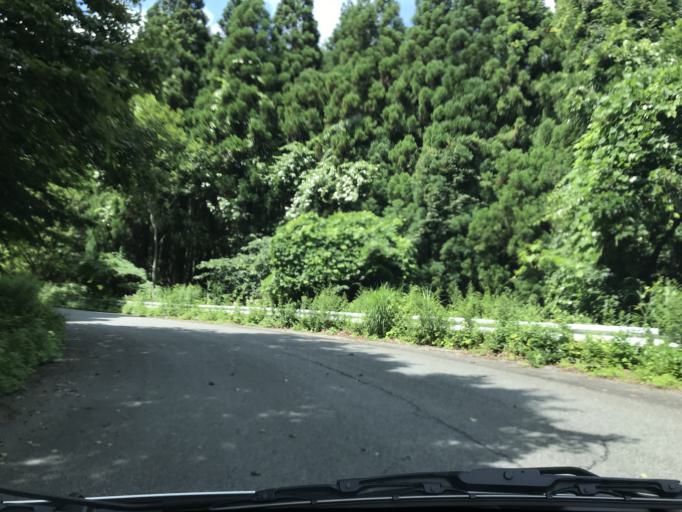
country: JP
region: Iwate
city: Tono
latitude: 39.0932
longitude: 141.4091
